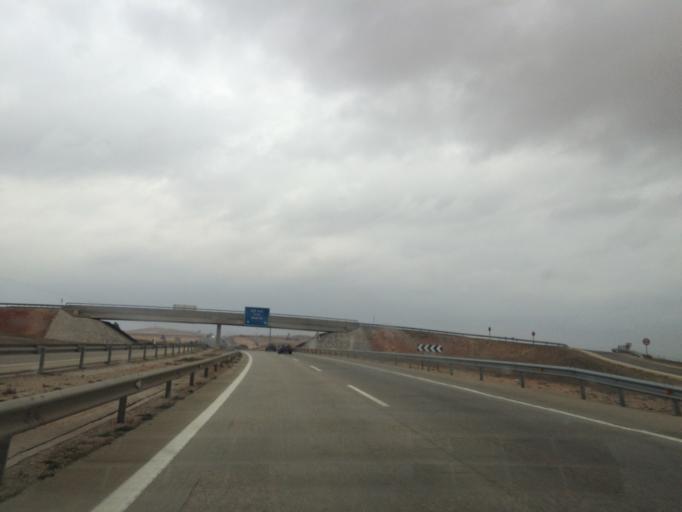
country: ES
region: Castille-La Mancha
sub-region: Province of Toledo
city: Turleque
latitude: 39.5716
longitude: -3.5141
